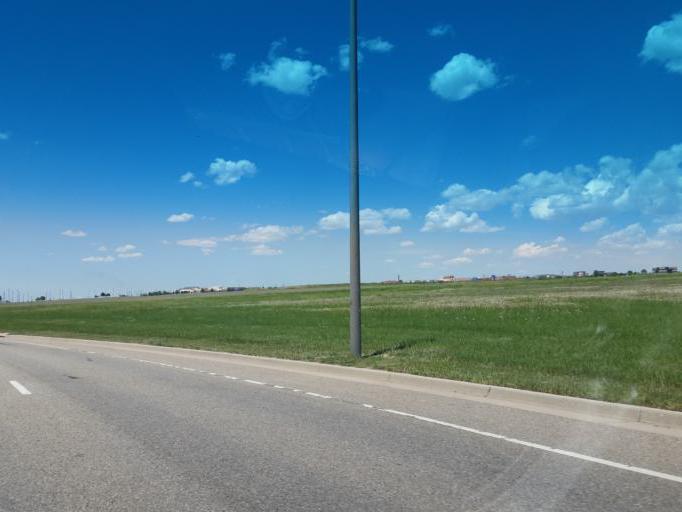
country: US
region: Colorado
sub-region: Larimer County
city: Loveland
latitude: 40.4195
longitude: -105.0002
